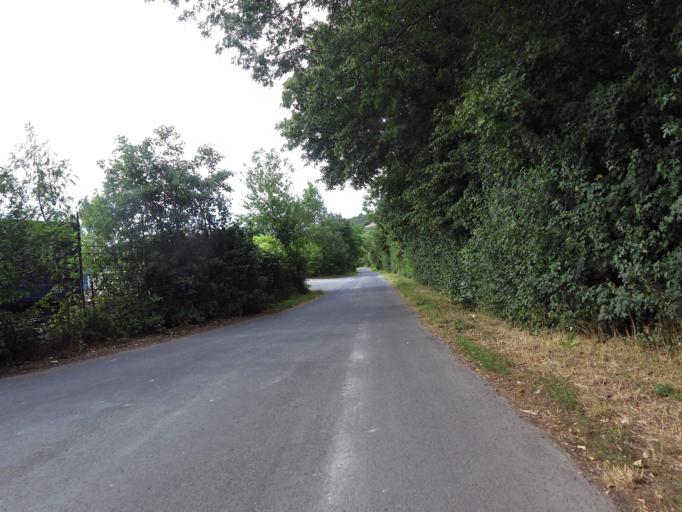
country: DE
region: Bavaria
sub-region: Regierungsbezirk Unterfranken
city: Randersacker
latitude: 49.7548
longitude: 9.9783
